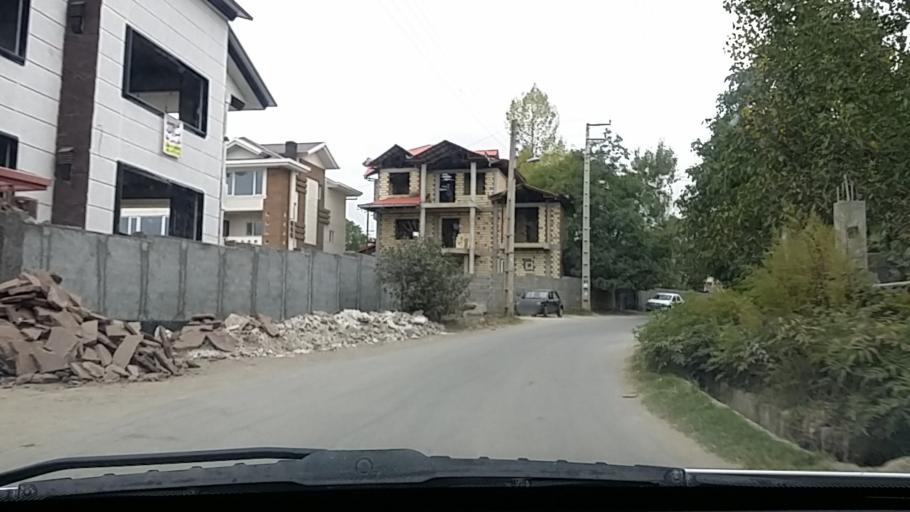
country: IR
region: Mazandaran
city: `Abbasabad
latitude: 36.5119
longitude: 51.1641
